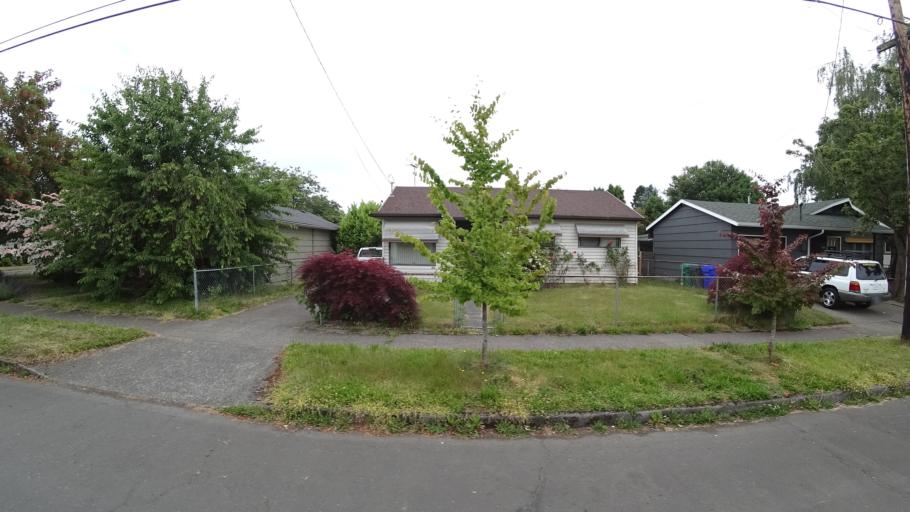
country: US
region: Oregon
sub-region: Multnomah County
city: Lents
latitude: 45.5120
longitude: -122.5751
